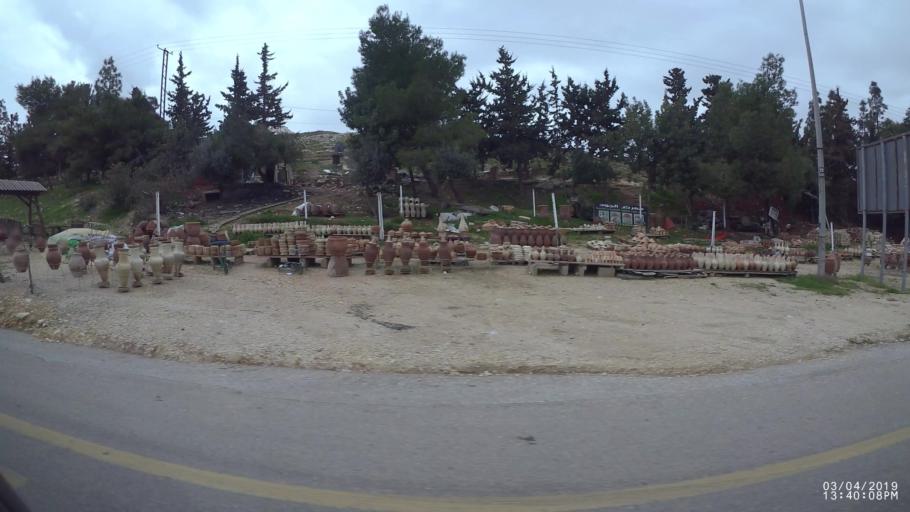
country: JO
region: Amman
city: Wadi as Sir
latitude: 31.9319
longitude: 35.8571
